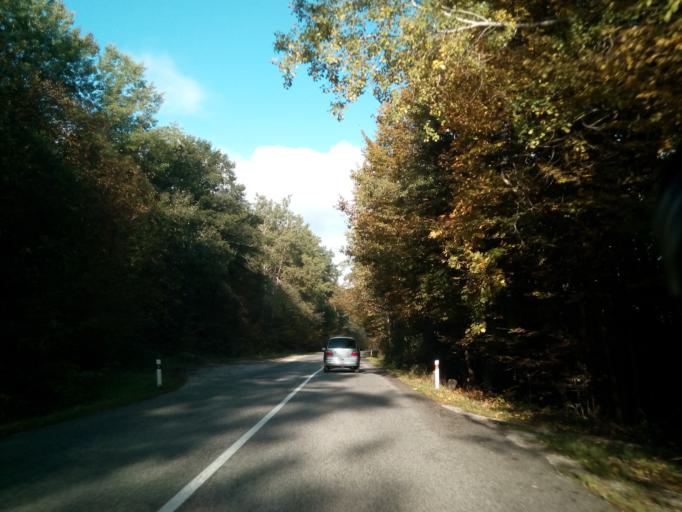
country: SK
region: Kosicky
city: Gelnica
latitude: 48.9102
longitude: 20.9568
